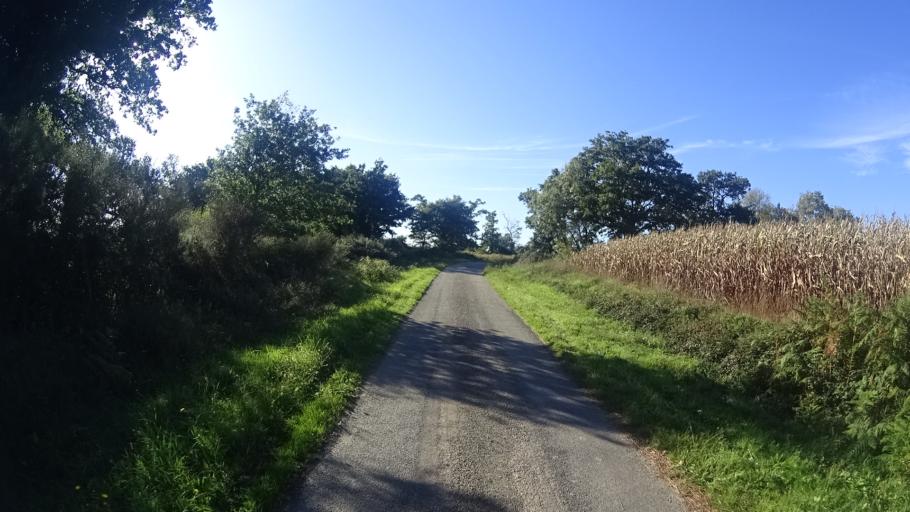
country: FR
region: Brittany
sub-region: Departement du Morbihan
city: Saint-Vincent-sur-Oust
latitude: 47.7022
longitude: -2.1760
